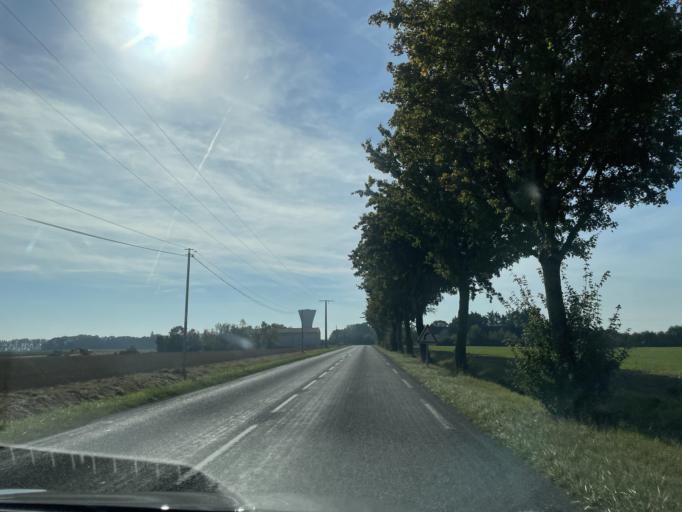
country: FR
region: Ile-de-France
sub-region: Departement de Seine-et-Marne
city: Coulommiers
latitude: 48.8514
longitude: 3.0903
